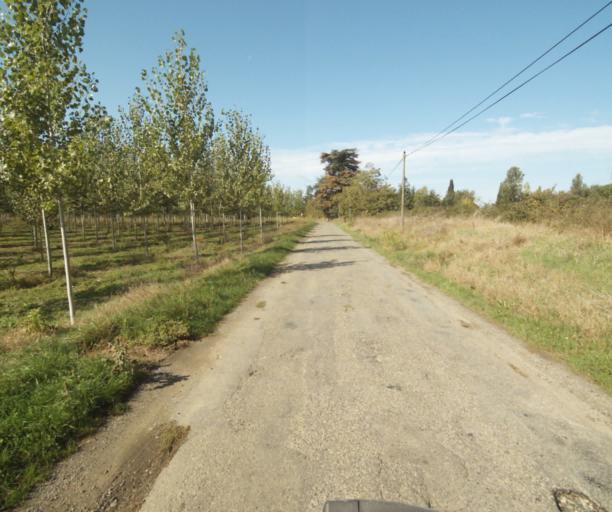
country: FR
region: Midi-Pyrenees
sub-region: Departement du Tarn-et-Garonne
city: Verdun-sur-Garonne
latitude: 43.8693
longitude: 1.2400
